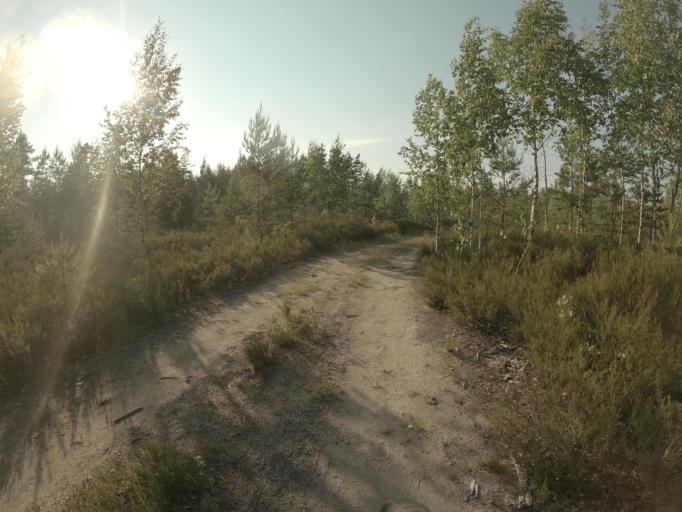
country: RU
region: Leningrad
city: Yakovlevo
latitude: 60.4435
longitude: 29.2399
